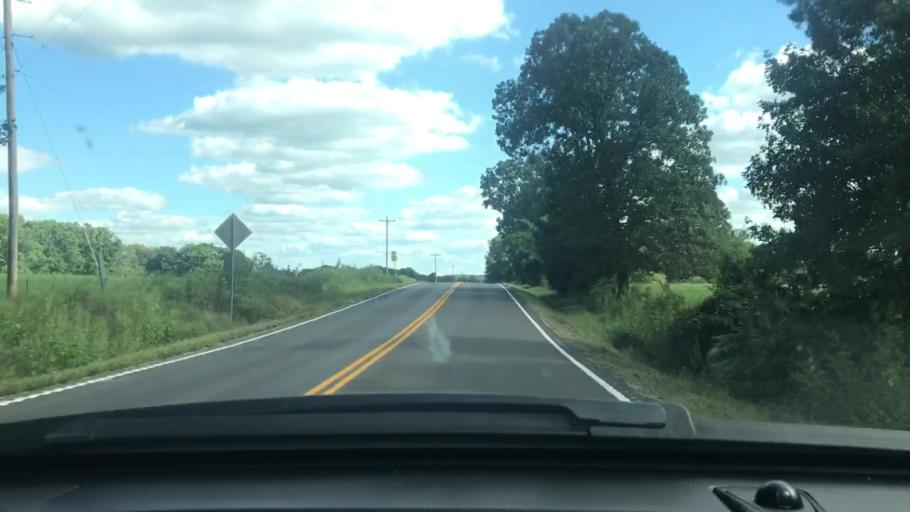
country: US
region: Missouri
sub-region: Wright County
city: Mountain Grove
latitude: 37.2991
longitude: -92.3118
